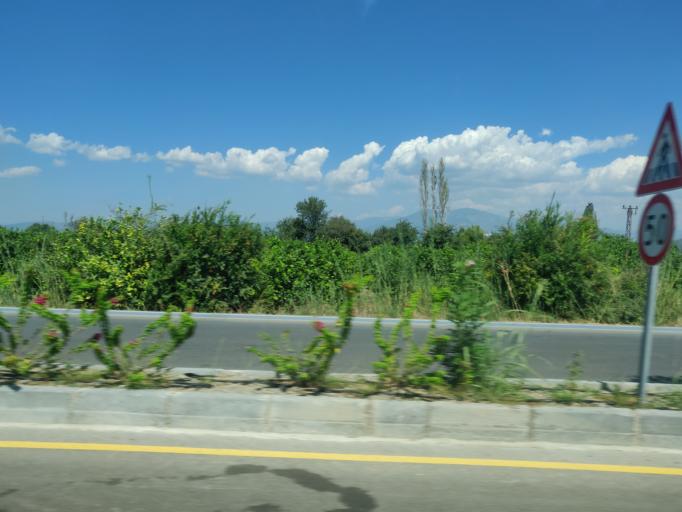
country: TR
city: Dalyan
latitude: 36.8393
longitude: 28.6588
